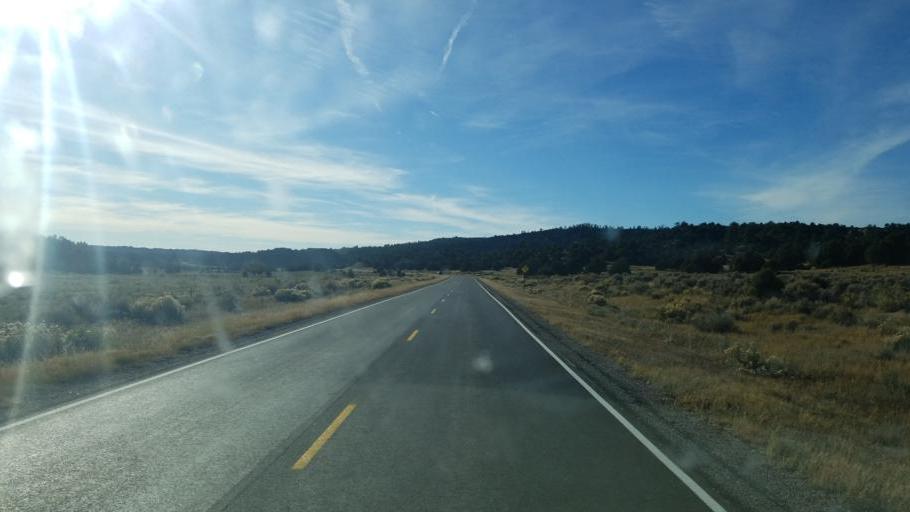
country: US
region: New Mexico
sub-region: Rio Arriba County
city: Dulce
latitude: 36.7892
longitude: -107.0553
